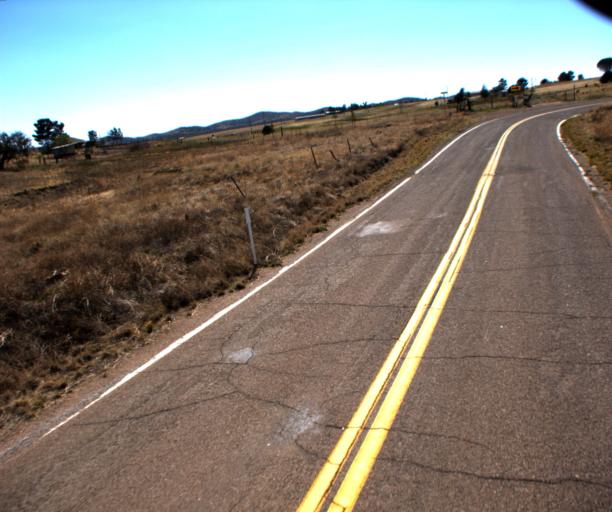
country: US
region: Arizona
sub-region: Cochise County
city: Huachuca City
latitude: 31.6008
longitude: -110.5777
